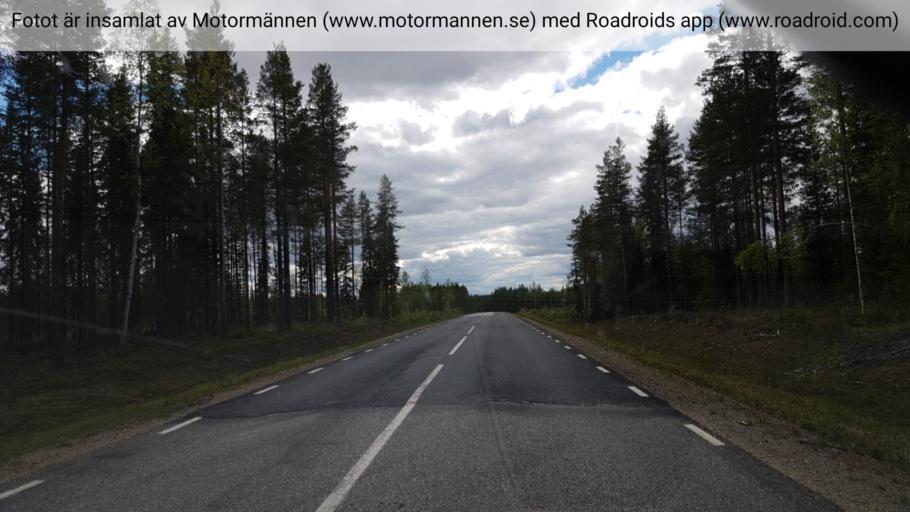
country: SE
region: Vaesterbotten
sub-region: Skelleftea Kommun
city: Langsele
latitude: 64.6529
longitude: 20.0073
